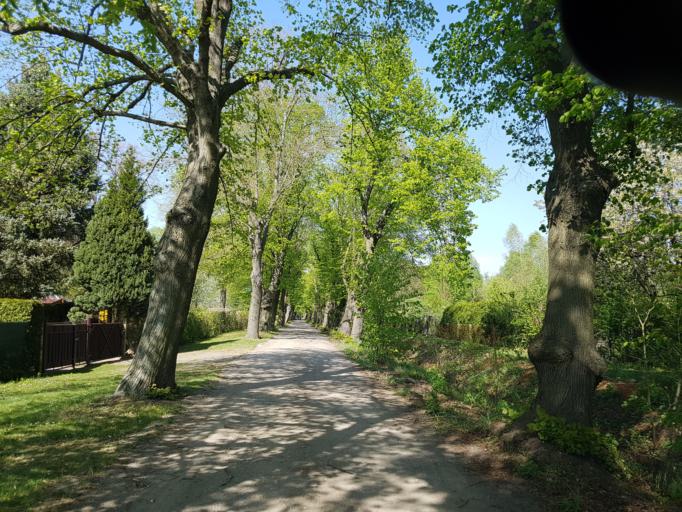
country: DE
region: Brandenburg
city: Finsterwalde
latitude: 51.6266
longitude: 13.6940
